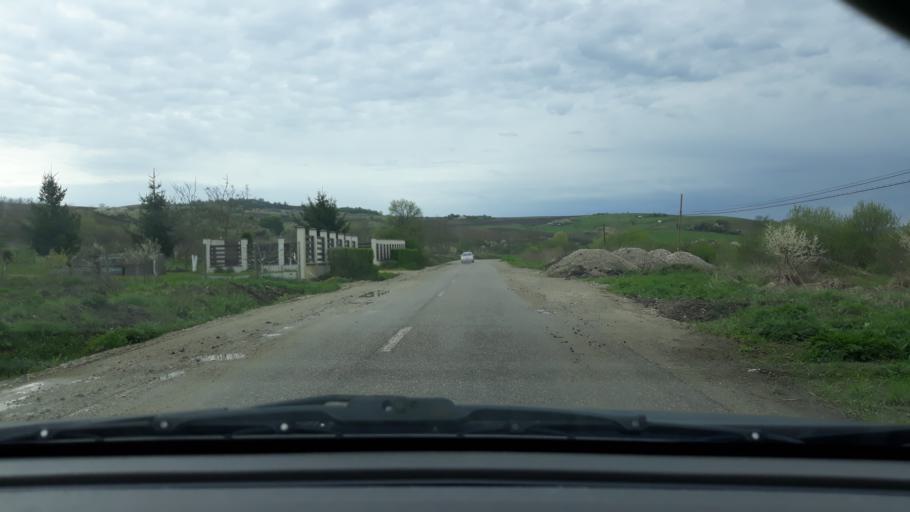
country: RO
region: Salaj
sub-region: Comuna Cehu Silvaniei
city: Cehu Silvaniei
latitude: 47.3939
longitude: 23.1536
